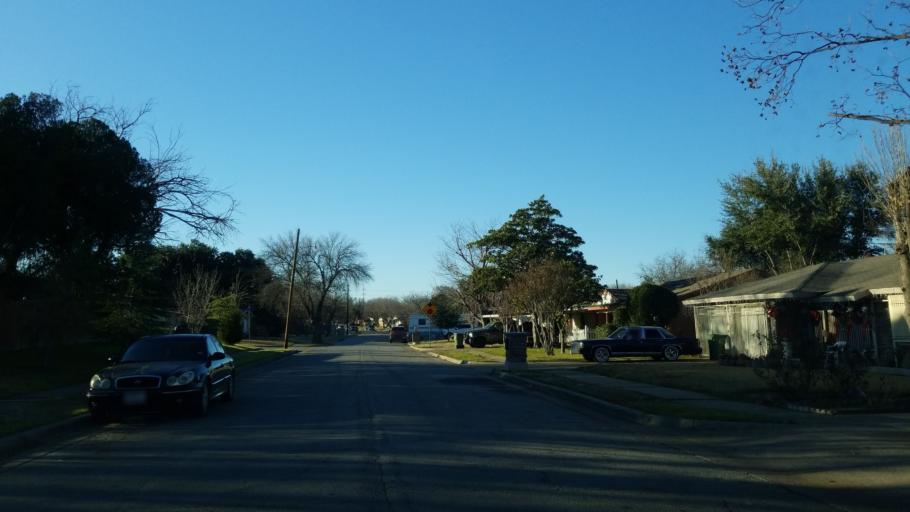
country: US
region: Texas
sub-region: Tarrant County
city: Arlington
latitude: 32.7292
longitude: -97.0664
